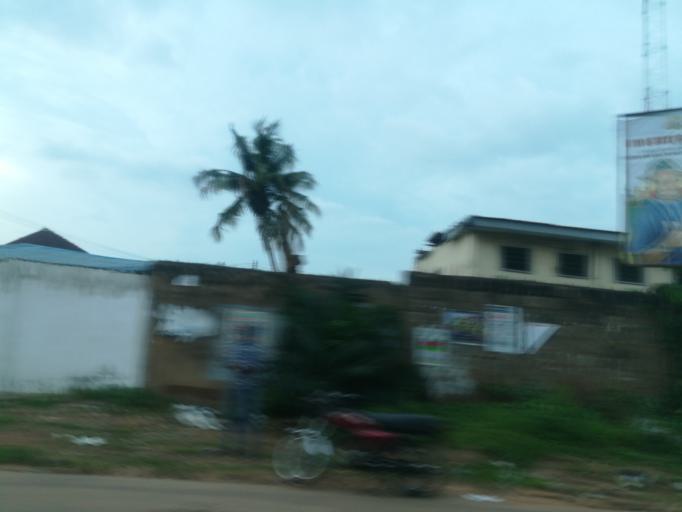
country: NG
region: Oyo
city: Ibadan
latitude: 7.4256
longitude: 3.9093
